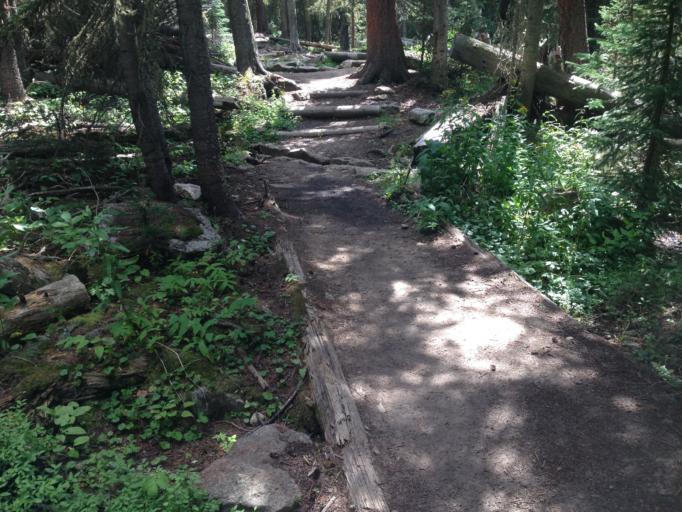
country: US
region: Colorado
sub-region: Larimer County
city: Estes Park
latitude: 40.1849
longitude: -105.5864
